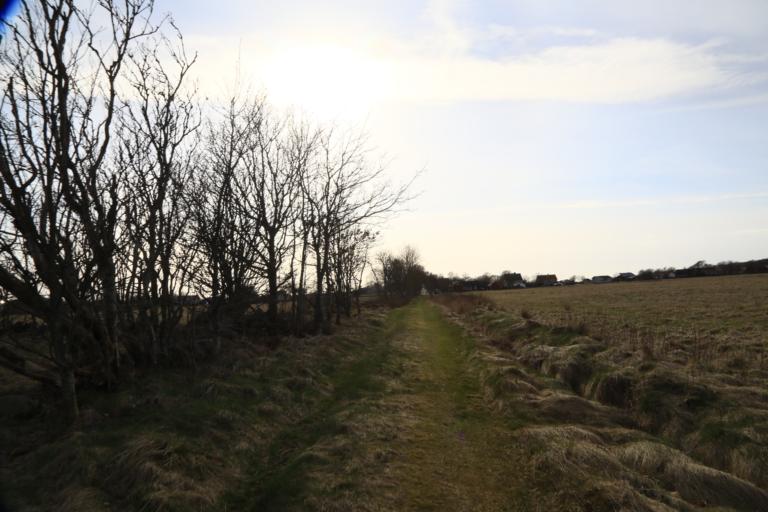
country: SE
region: Halland
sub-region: Varbergs Kommun
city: Varberg
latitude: 57.1216
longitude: 12.2186
